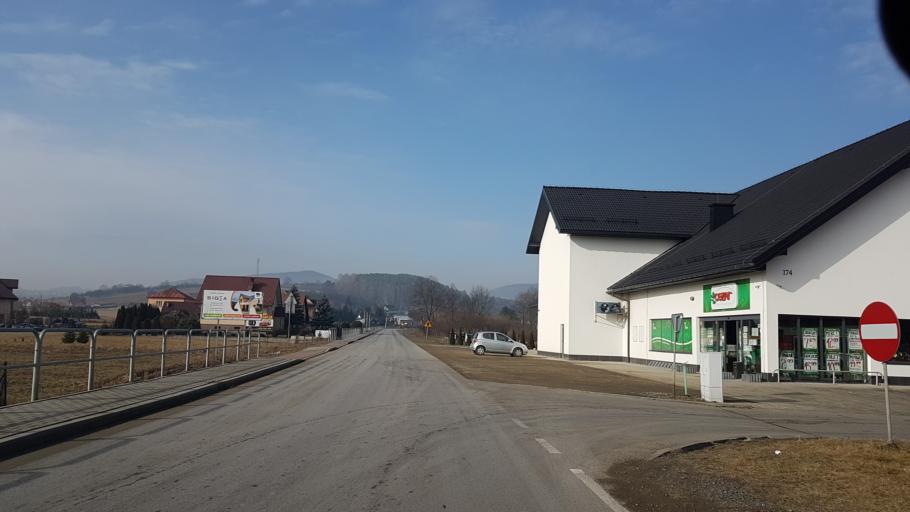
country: PL
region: Lesser Poland Voivodeship
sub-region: Powiat nowosadecki
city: Olszana
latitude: 49.5951
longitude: 20.5334
